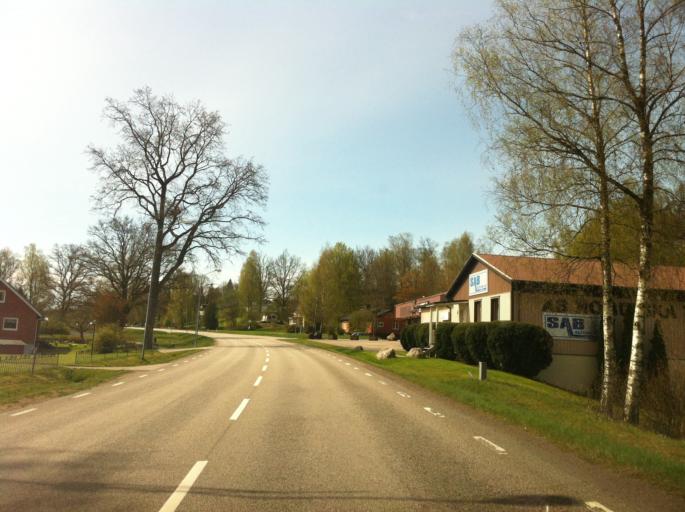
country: SE
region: Vaestra Goetaland
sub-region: Marks Kommun
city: Fritsla
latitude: 57.3483
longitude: 12.8953
